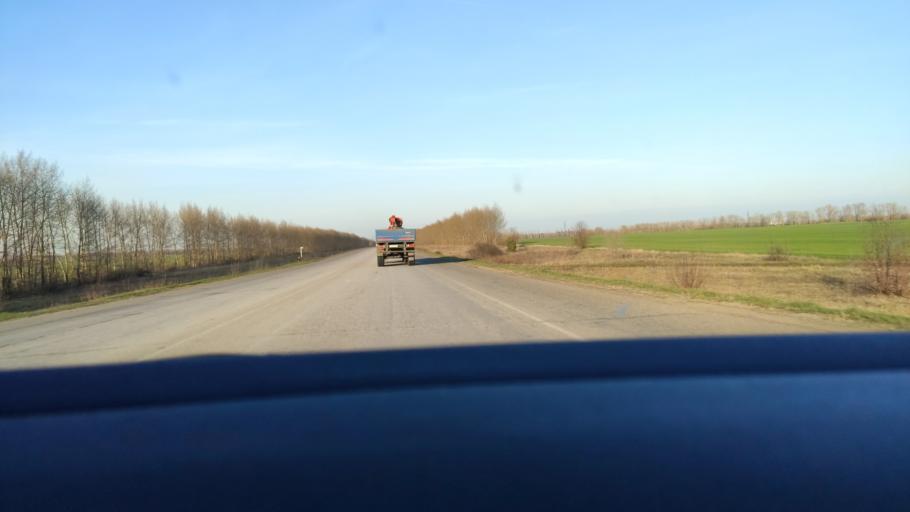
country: RU
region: Voronezj
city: Kolodeznyy
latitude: 51.4116
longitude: 39.2546
